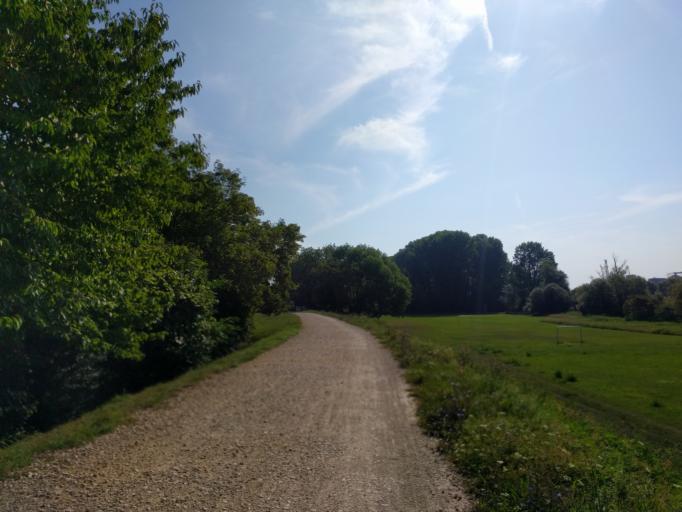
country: DE
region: Bavaria
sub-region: Upper Palatinate
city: Regensburg
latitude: 49.0224
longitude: 12.1156
